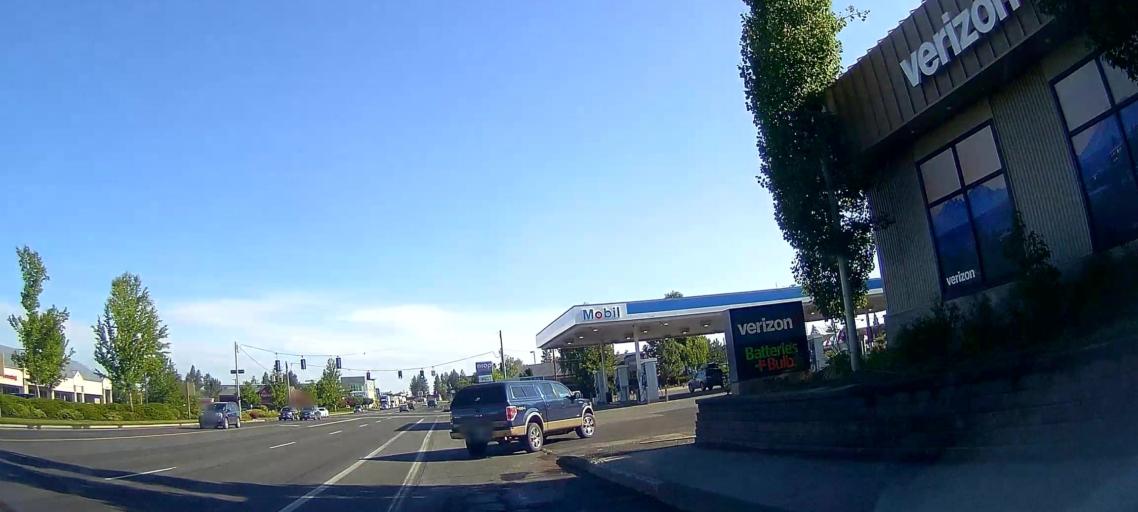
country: US
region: Oregon
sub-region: Deschutes County
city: Bend
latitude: 44.0830
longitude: -121.3052
